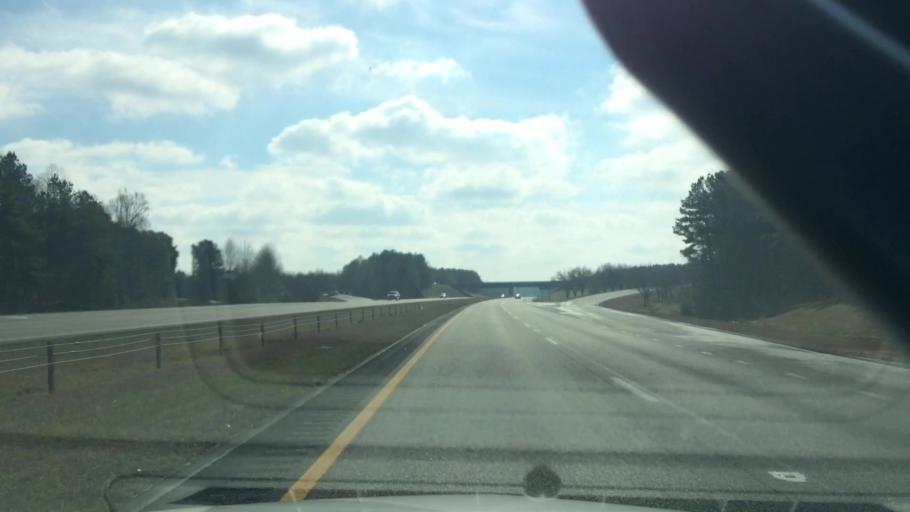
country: US
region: North Carolina
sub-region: Duplin County
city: Wallace
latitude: 34.6913
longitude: -77.9455
